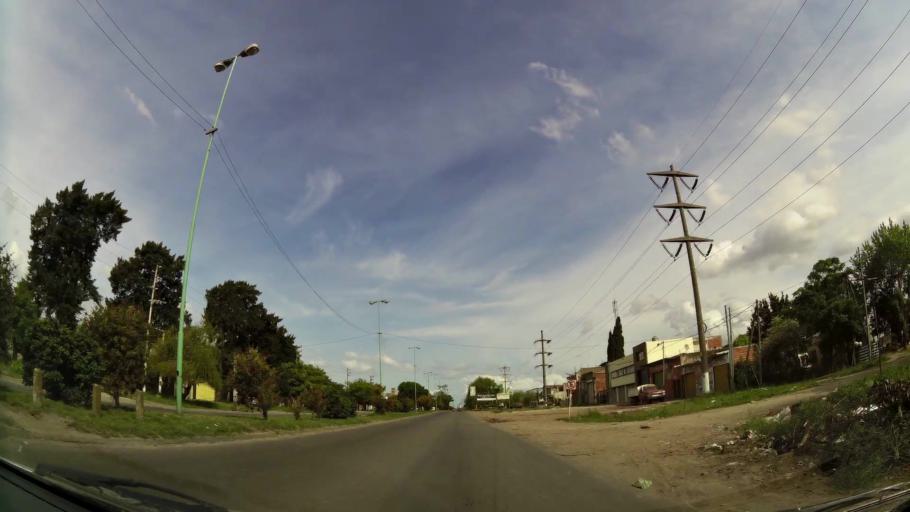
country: AR
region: Buenos Aires
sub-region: Partido de Quilmes
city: Quilmes
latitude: -34.7667
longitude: -58.2484
